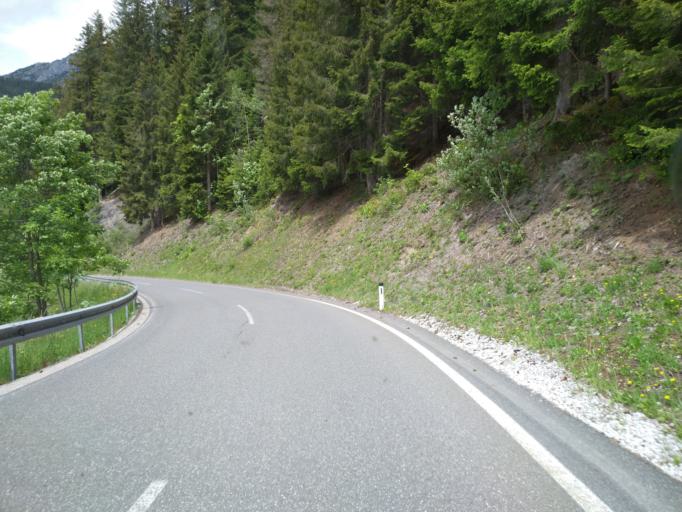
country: AT
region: Salzburg
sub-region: Politischer Bezirk Sankt Johann im Pongau
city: Filzmoos
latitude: 47.4339
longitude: 13.5803
